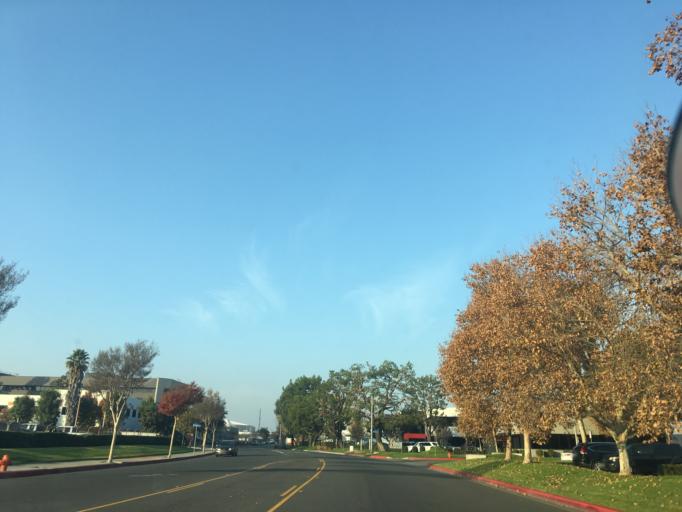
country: US
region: California
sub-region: Orange County
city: Orange
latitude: 33.7976
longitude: -117.8737
